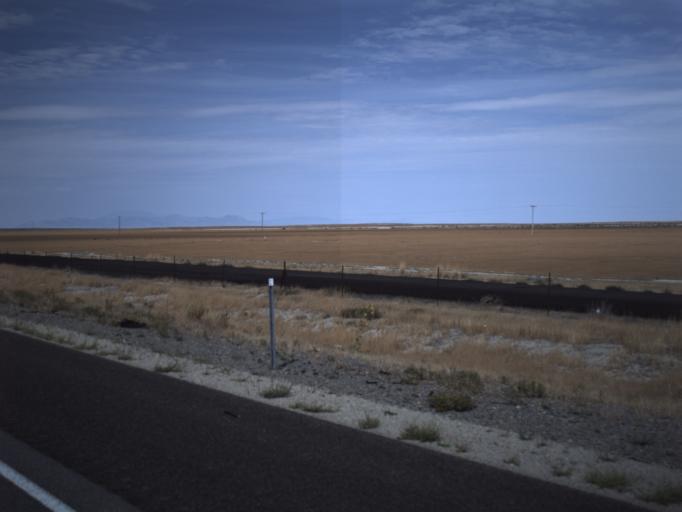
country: US
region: Utah
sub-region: Tooele County
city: Grantsville
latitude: 40.7269
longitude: -113.2216
